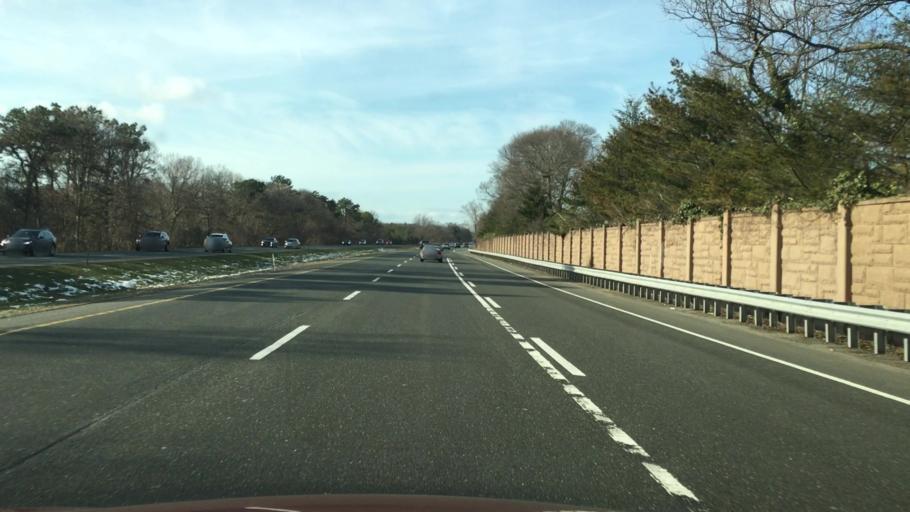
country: US
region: New York
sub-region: Suffolk County
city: Centereach
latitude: 40.8643
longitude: -73.0692
